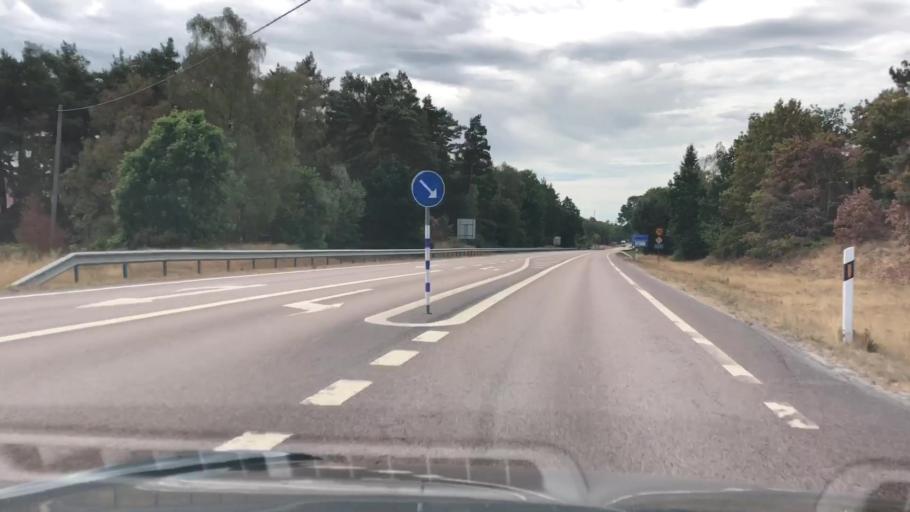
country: SE
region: Kalmar
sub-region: Torsas Kommun
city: Torsas
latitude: 56.3022
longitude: 16.0060
